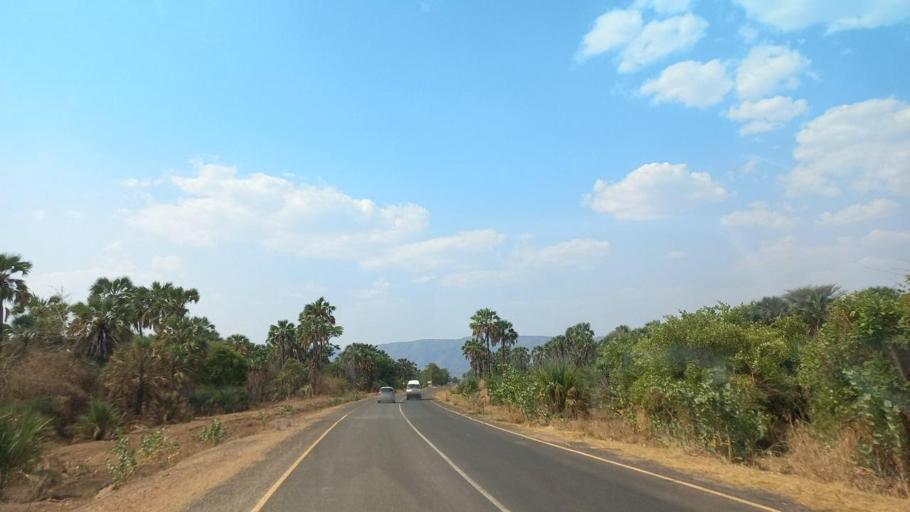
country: ZM
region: Lusaka
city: Luangwa
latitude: -15.0916
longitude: 30.1926
